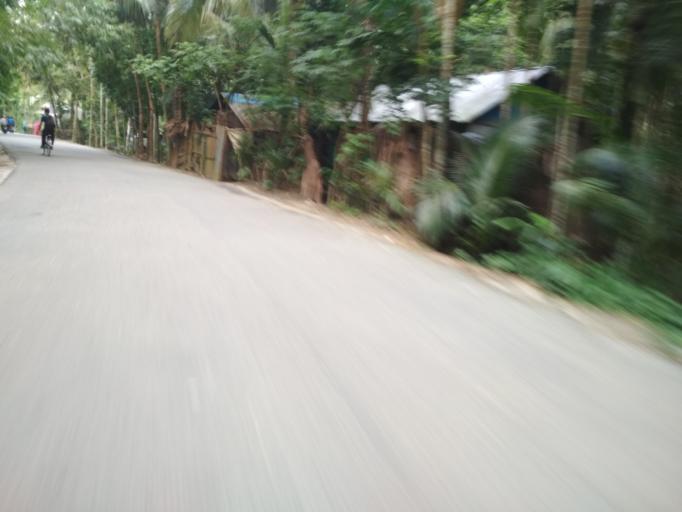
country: BD
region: Chittagong
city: Raipur
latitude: 23.0056
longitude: 90.7138
